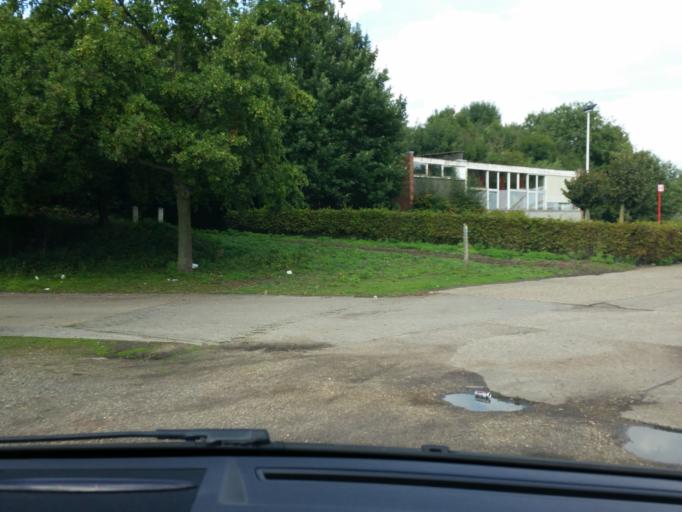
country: BE
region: Flanders
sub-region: Provincie Antwerpen
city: Borsbeek
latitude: 51.1868
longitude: 4.4805
